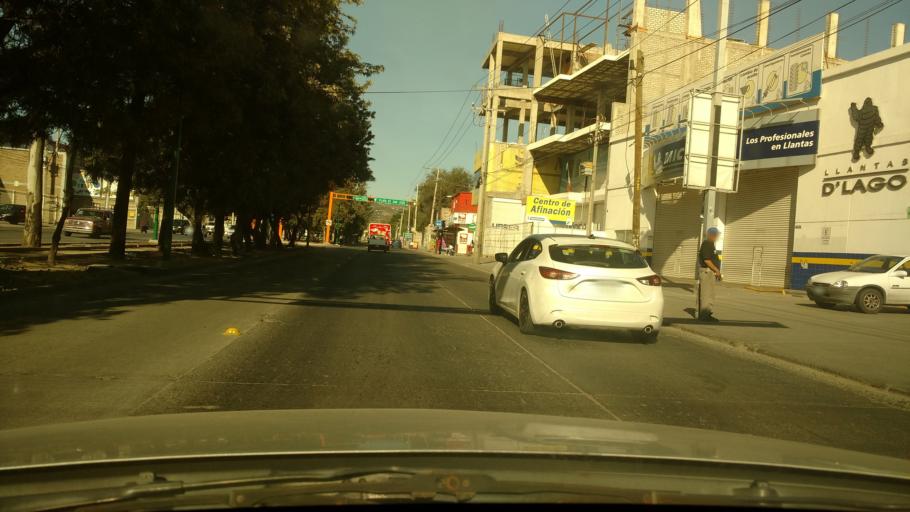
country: MX
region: Guanajuato
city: Leon
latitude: 21.1610
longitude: -101.6652
